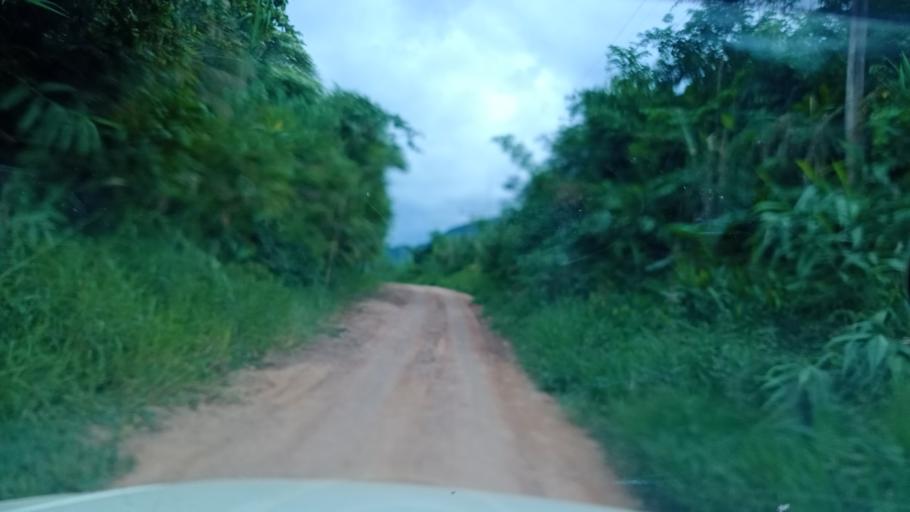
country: TH
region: Changwat Bueng Kan
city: Pak Khat
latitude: 18.7270
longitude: 103.2762
